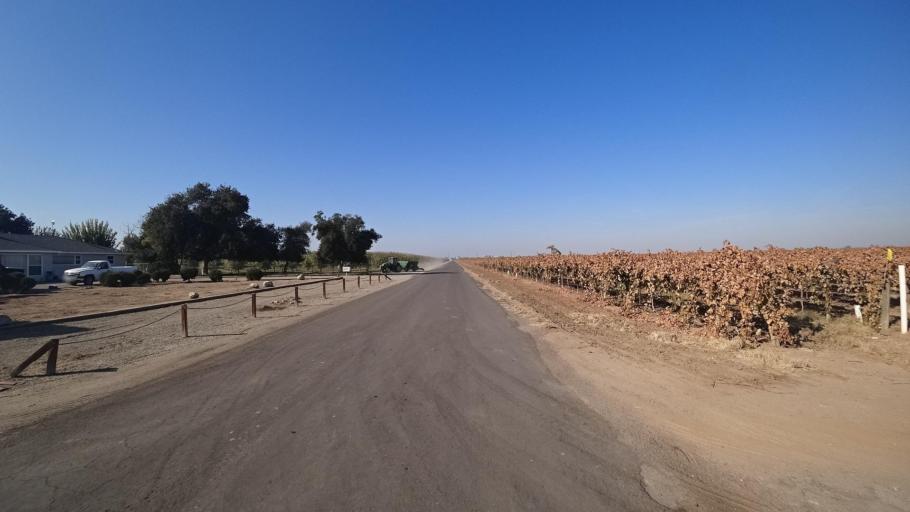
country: US
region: California
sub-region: Kern County
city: Delano
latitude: 35.7325
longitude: -119.2141
